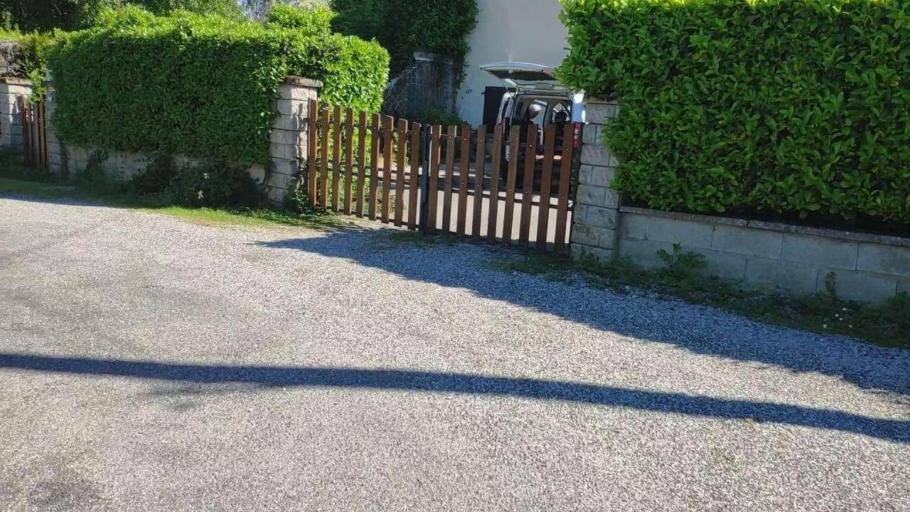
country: FR
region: Franche-Comte
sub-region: Departement du Jura
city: Perrigny
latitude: 46.7179
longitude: 5.5833
